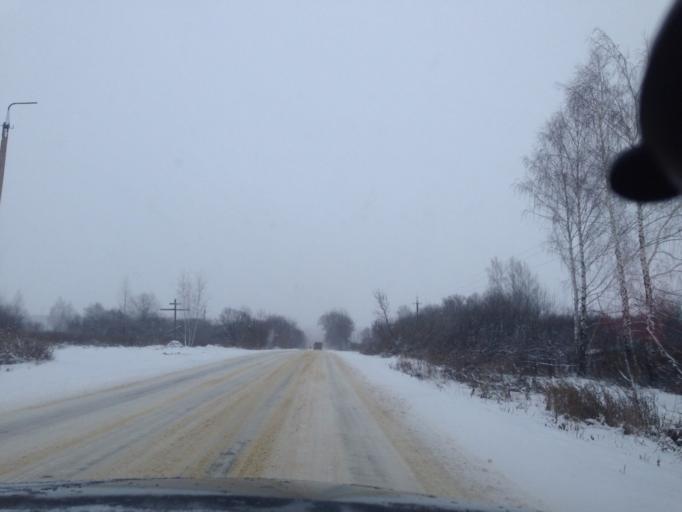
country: RU
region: Tula
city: Bolokhovo
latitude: 54.0827
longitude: 37.8398
